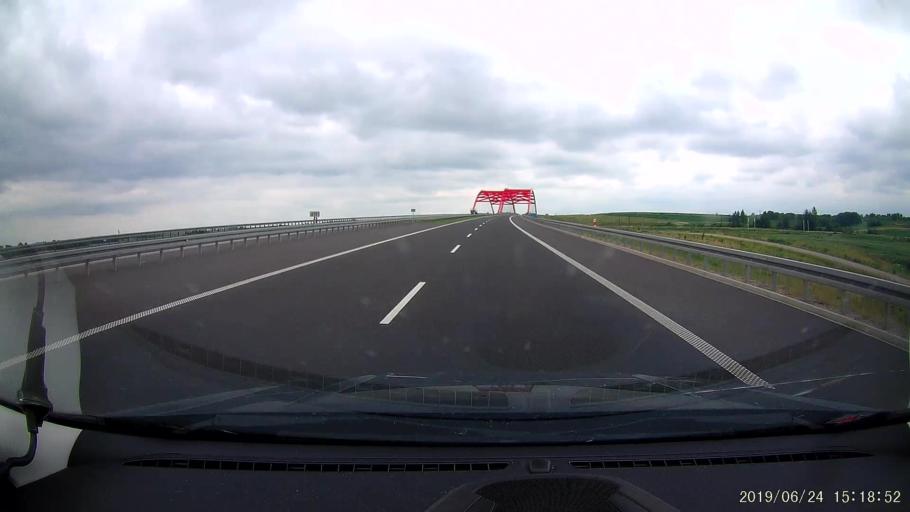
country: PL
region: Subcarpathian Voivodeship
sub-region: Powiat przeworski
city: Rozborz
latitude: 50.0660
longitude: 22.5614
